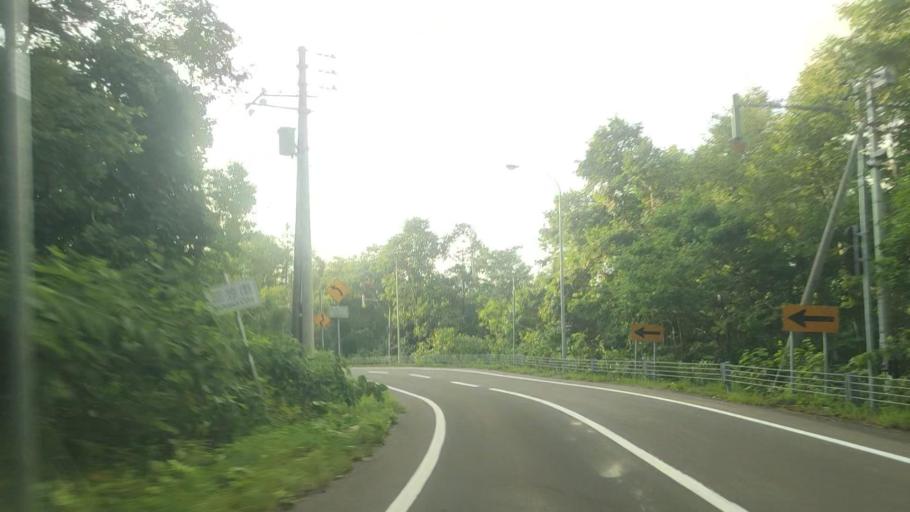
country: JP
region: Hokkaido
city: Bibai
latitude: 43.1672
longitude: 142.0806
